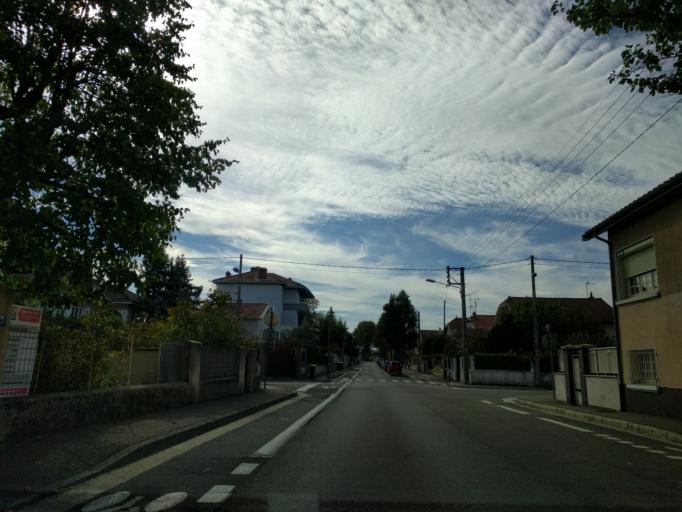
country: FR
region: Rhone-Alpes
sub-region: Departement du Rhone
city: Bron
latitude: 45.7377
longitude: 4.9108
